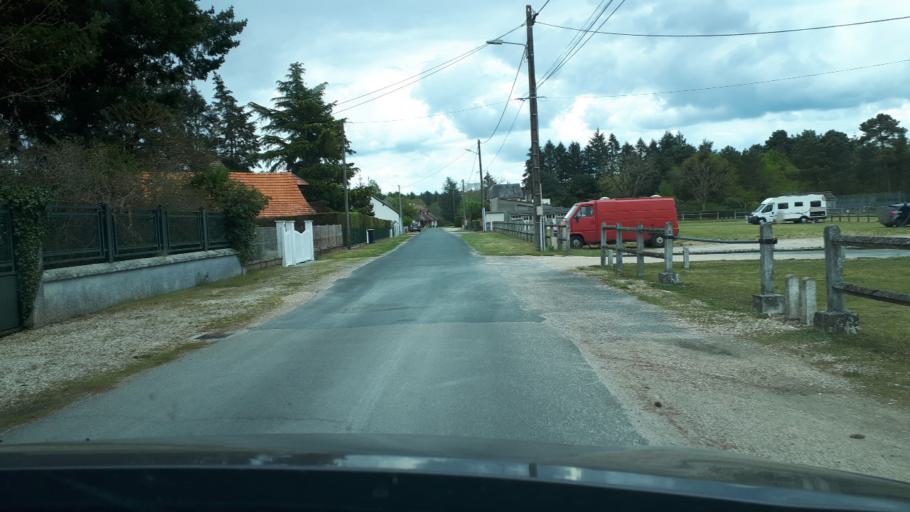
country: FR
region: Centre
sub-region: Departement du Loir-et-Cher
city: Souesmes
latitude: 47.5093
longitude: 2.1546
